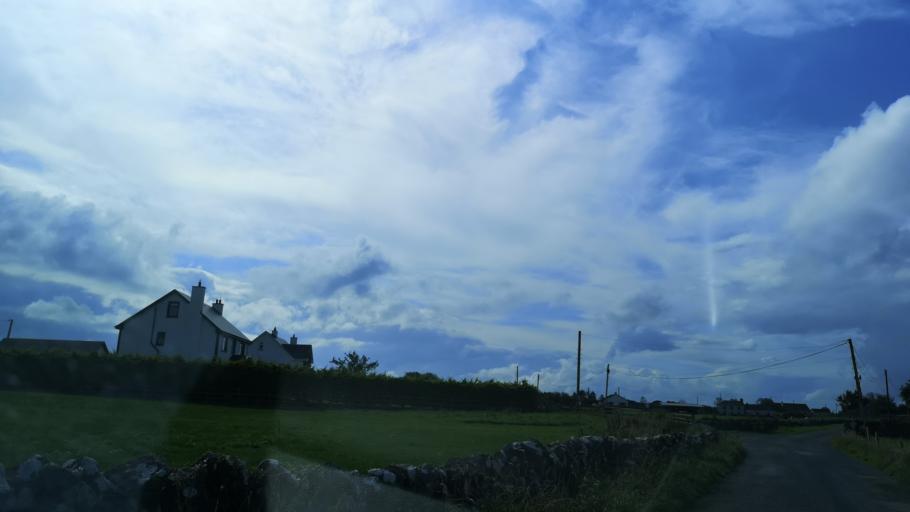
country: IE
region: Connaught
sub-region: County Galway
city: Athenry
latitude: 53.3122
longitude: -8.8064
